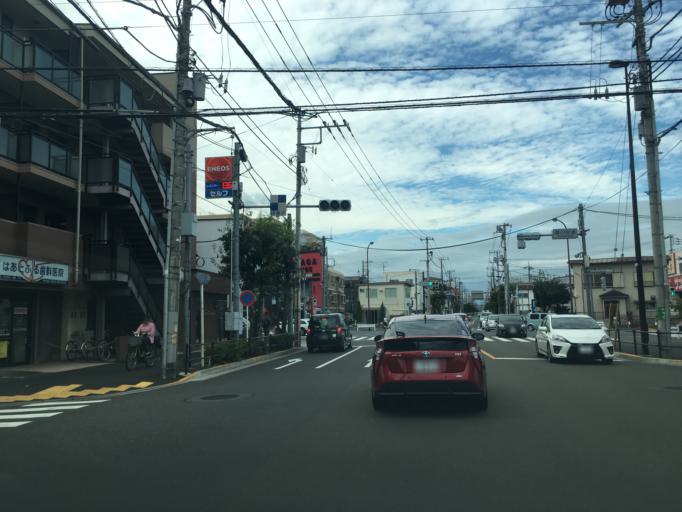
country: JP
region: Tokyo
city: Chofugaoka
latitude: 35.6509
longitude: 139.5370
